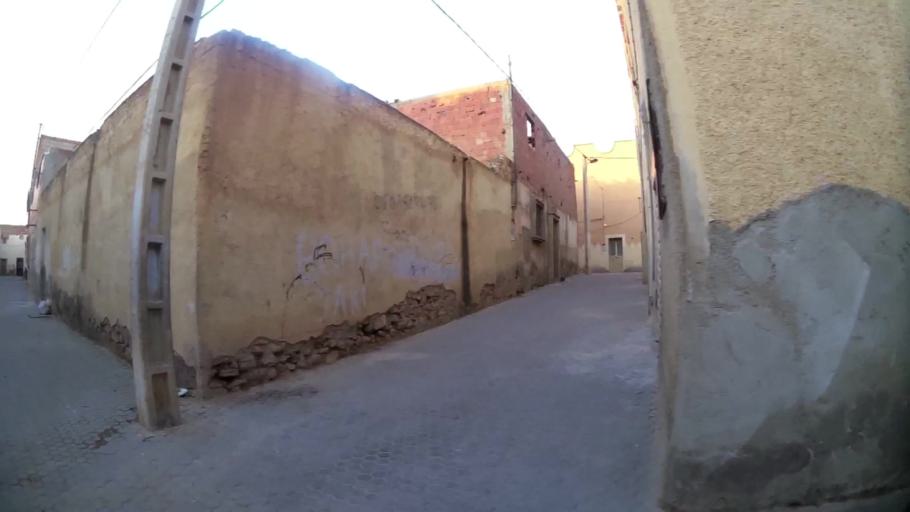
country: MA
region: Oriental
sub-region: Oujda-Angad
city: Oujda
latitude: 34.6993
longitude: -1.9243
